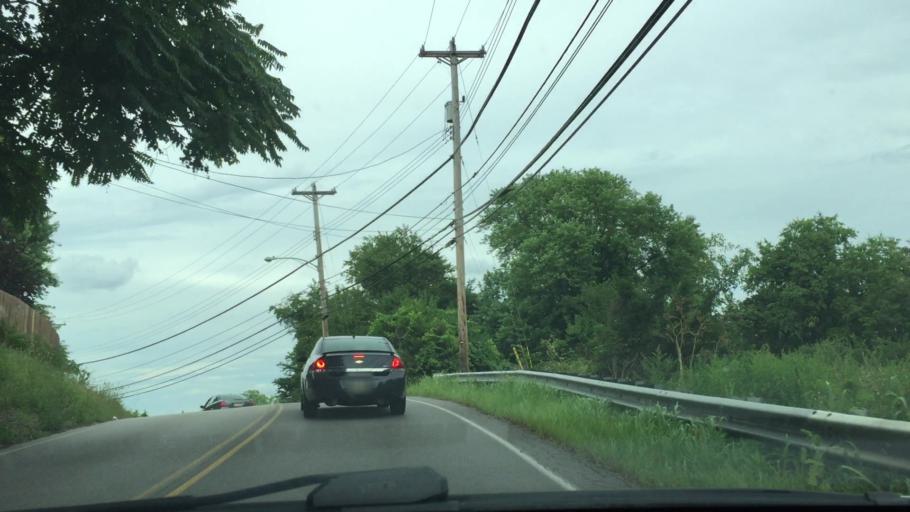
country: US
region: Pennsylvania
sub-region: Allegheny County
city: McKees Rocks
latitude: 40.4612
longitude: -80.1064
